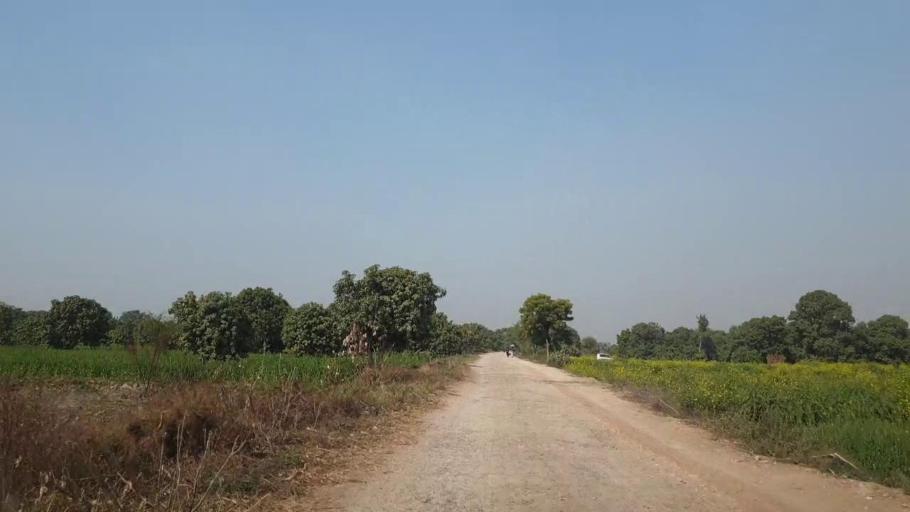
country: PK
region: Sindh
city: Tando Allahyar
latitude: 25.4843
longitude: 68.8051
